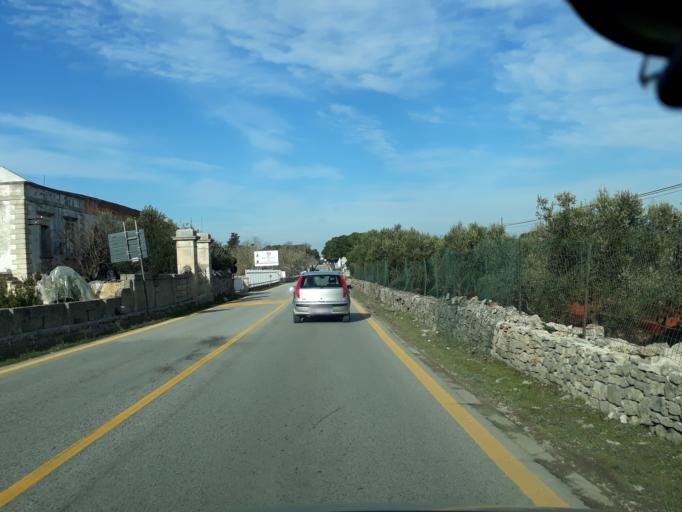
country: IT
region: Apulia
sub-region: Provincia di Taranto
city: Martina Franca
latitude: 40.7177
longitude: 17.3328
